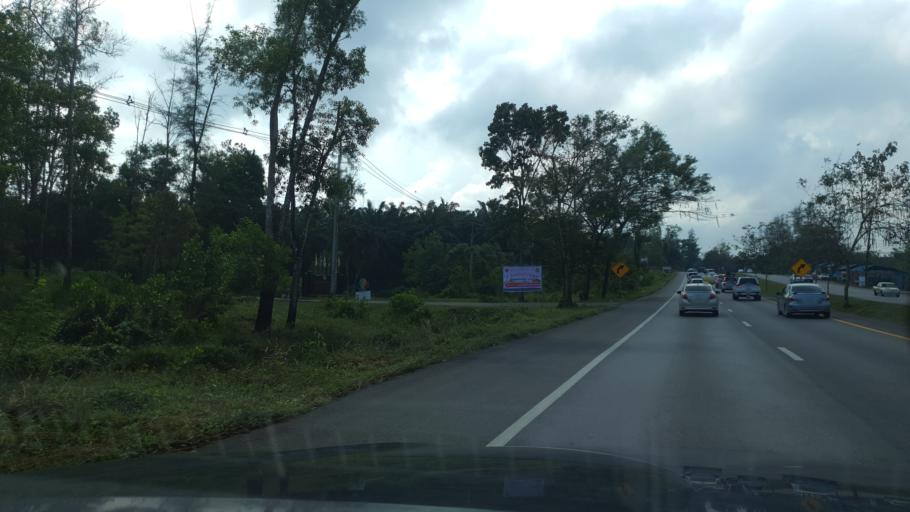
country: TH
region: Chumphon
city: Pathio
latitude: 10.8181
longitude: 99.2112
